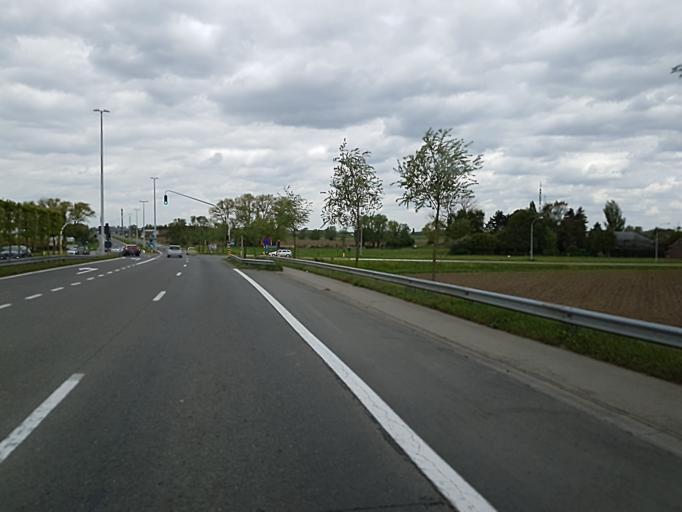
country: BE
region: Flanders
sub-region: Provincie West-Vlaanderen
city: Menen
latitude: 50.8103
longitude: 3.1344
